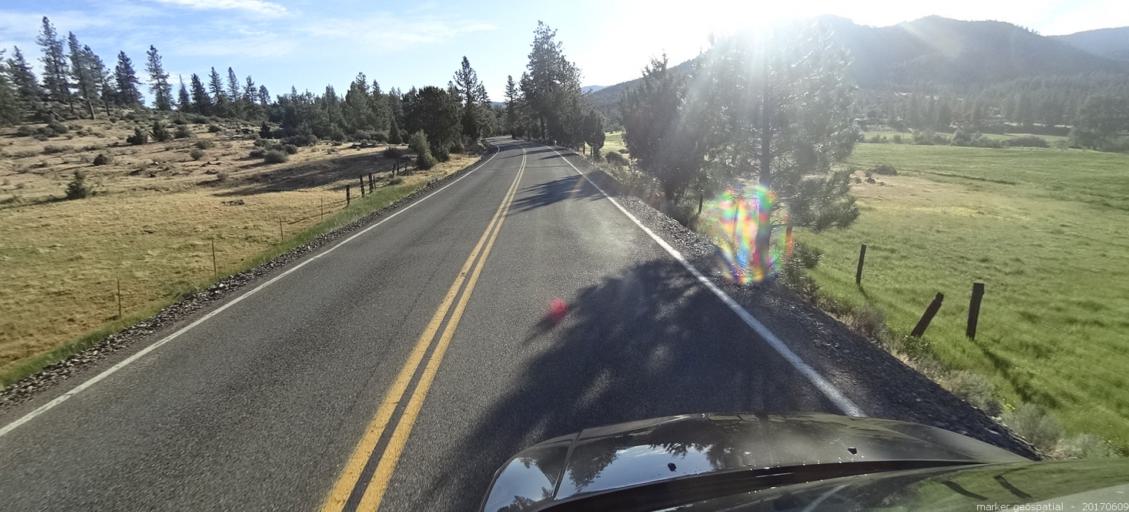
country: US
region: California
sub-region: Siskiyou County
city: Weed
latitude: 41.3550
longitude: -122.7250
